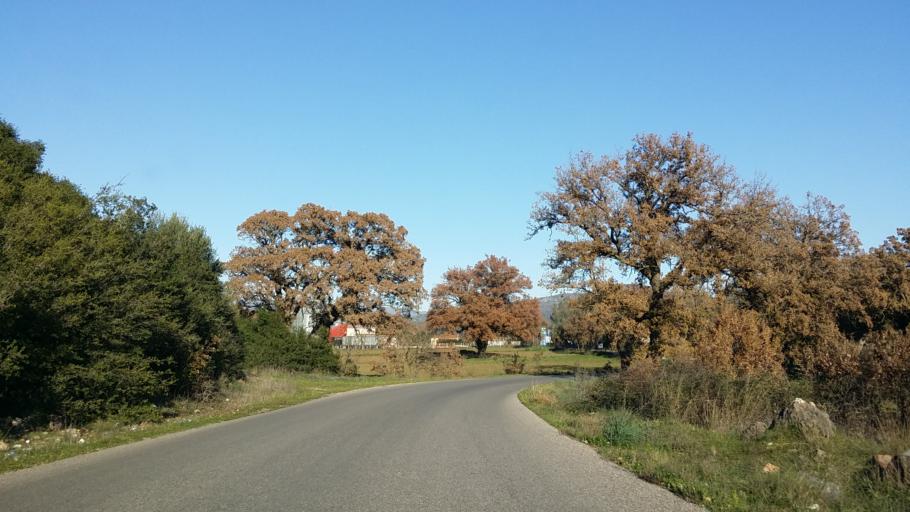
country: GR
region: West Greece
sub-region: Nomos Aitolias kai Akarnanias
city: Fitiai
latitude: 38.6159
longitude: 21.1420
